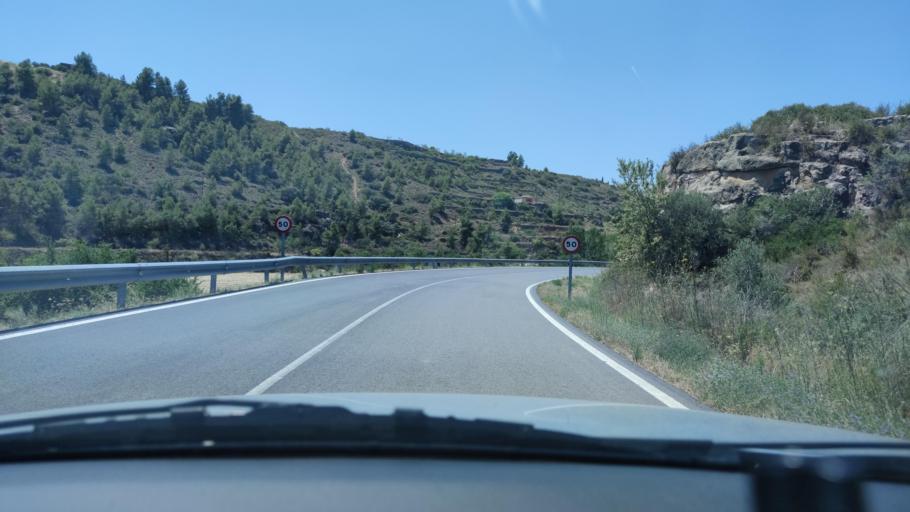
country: ES
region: Catalonia
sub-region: Provincia de Lleida
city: el Cogul
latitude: 41.4122
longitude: 0.6908
